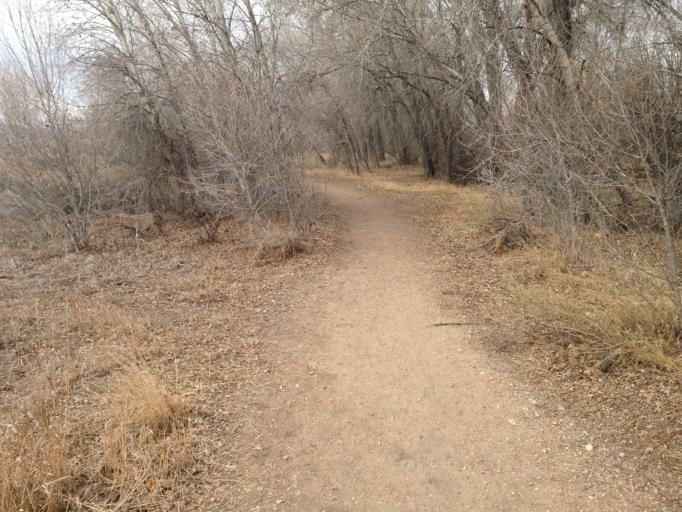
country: US
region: Colorado
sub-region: Larimer County
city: Fort Collins
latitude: 40.5358
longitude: -104.9988
